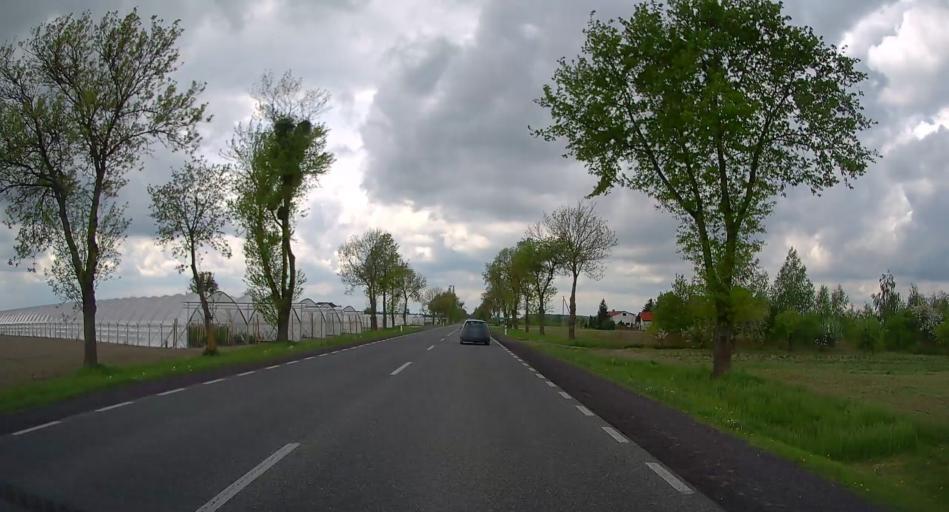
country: PL
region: Masovian Voivodeship
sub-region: Powiat plonski
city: Zaluski
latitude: 52.4411
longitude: 20.4864
